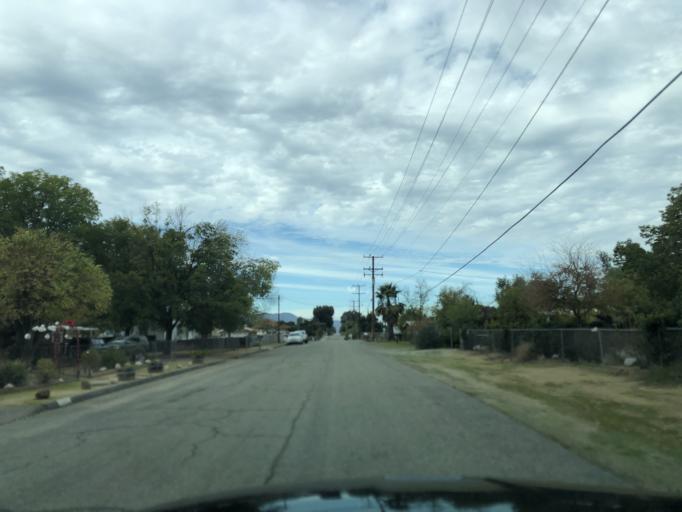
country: US
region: California
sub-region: Riverside County
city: Wildomar
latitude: 33.6053
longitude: -117.2827
